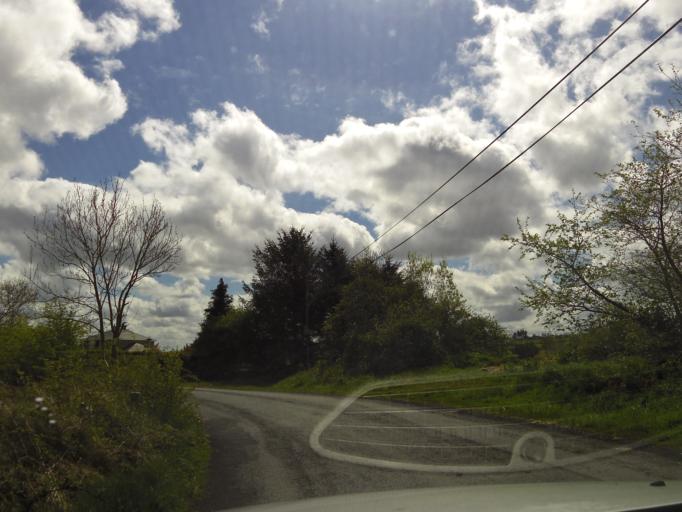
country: IE
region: Connaught
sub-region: Maigh Eo
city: Claremorris
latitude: 53.7778
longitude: -8.9609
